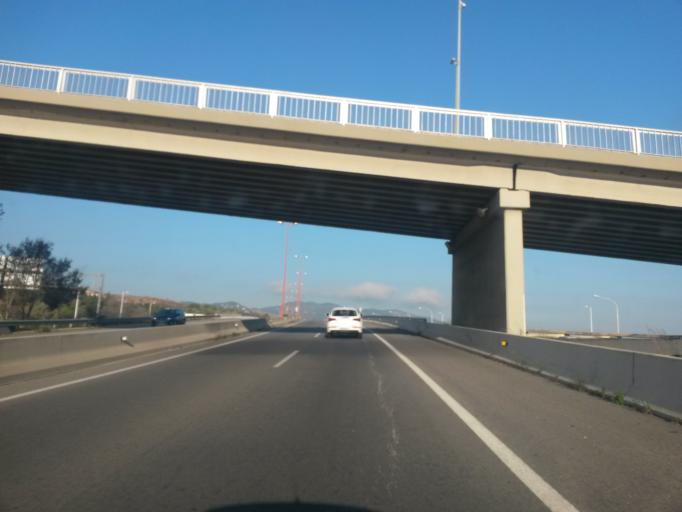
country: ES
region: Catalonia
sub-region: Provincia de Barcelona
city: Montgat
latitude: 41.4731
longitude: 2.2819
